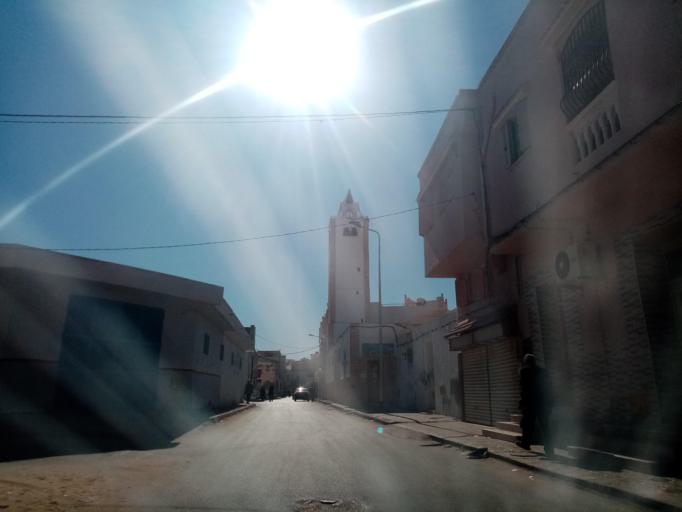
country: TN
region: Qabis
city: Gabes
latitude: 33.8802
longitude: 10.0895
